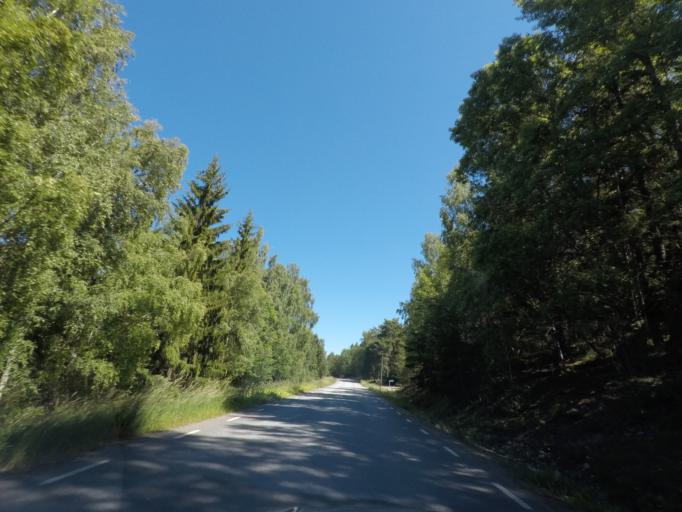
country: SE
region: Uppsala
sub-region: Enkopings Kommun
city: Enkoping
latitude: 59.7136
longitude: 17.0919
